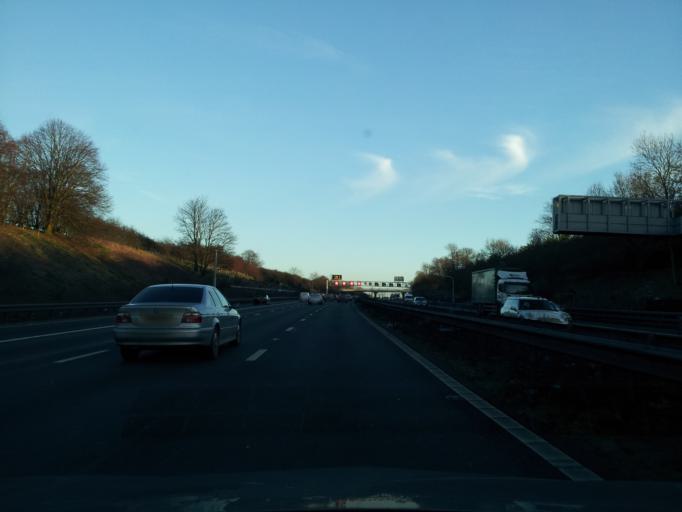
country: GB
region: England
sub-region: Central Bedfordshire
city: Ridgmont
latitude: 52.0176
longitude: -0.5679
